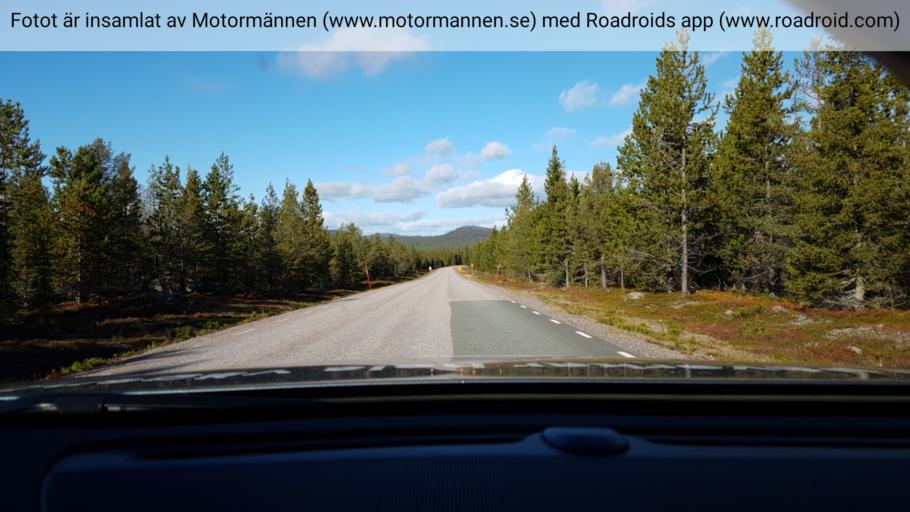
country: SE
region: Norrbotten
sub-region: Arjeplogs Kommun
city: Arjeplog
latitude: 65.8436
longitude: 18.4122
